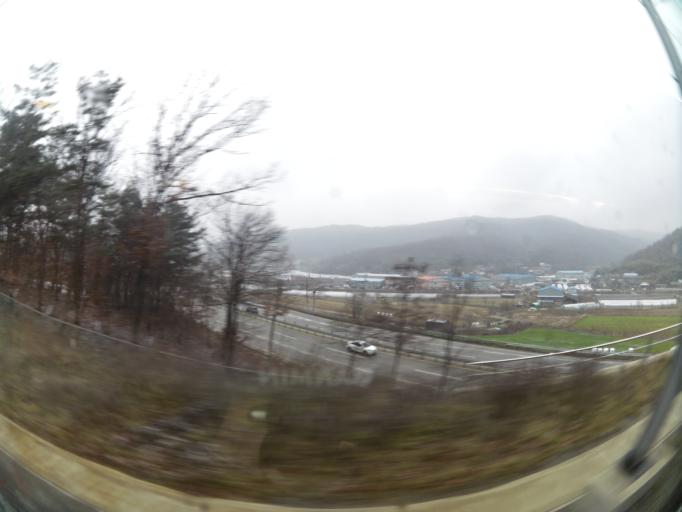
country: KR
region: Daegu
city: Daegu
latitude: 35.9124
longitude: 128.5038
